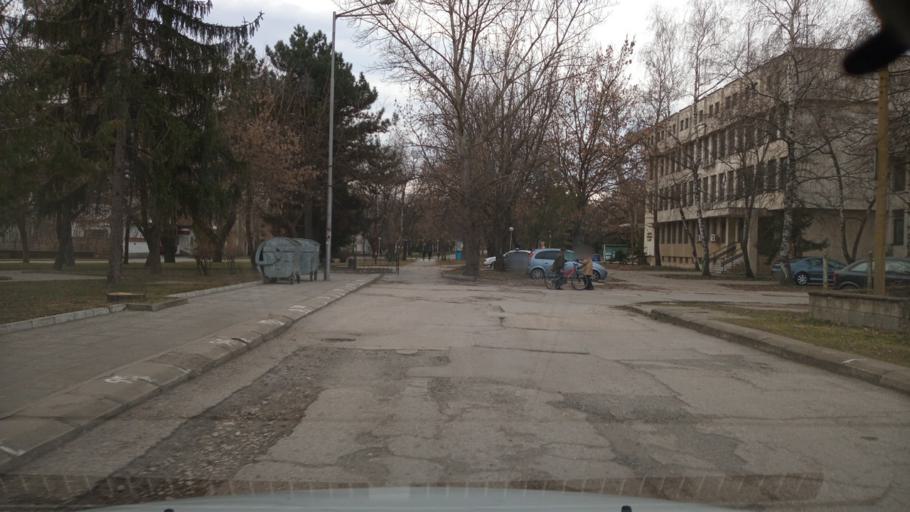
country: BG
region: Pleven
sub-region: Obshtina Belene
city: Belene
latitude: 43.6455
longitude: 25.1247
